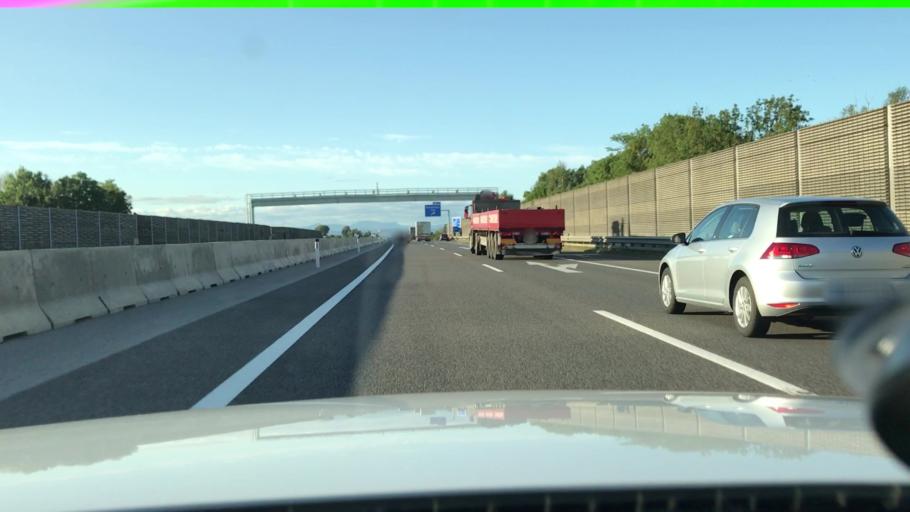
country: AT
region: Lower Austria
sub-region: Politischer Bezirk Sankt Polten
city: Herzogenburg
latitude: 48.2878
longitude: 15.7021
